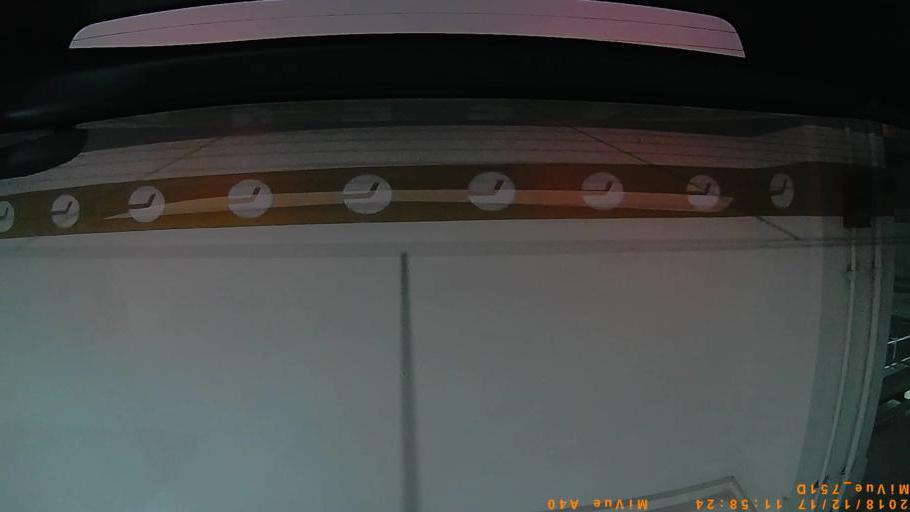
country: TW
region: Taiwan
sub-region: Hualien
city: Hualian
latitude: 23.9088
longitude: 121.5970
